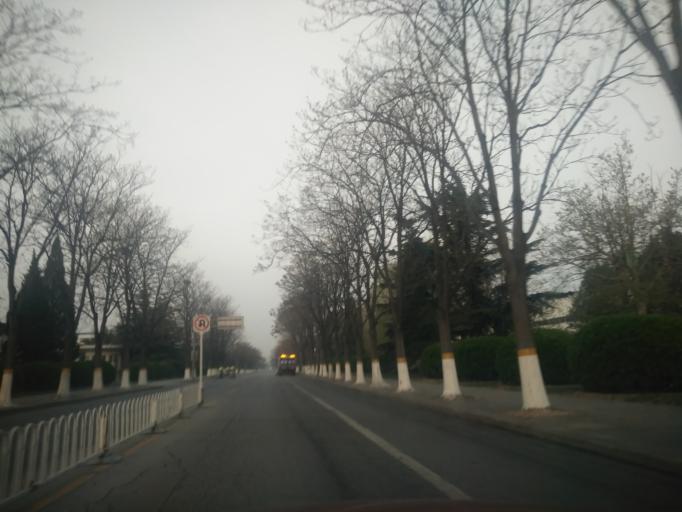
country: CN
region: Beijing
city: Jiugong
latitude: 39.8031
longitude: 116.5090
